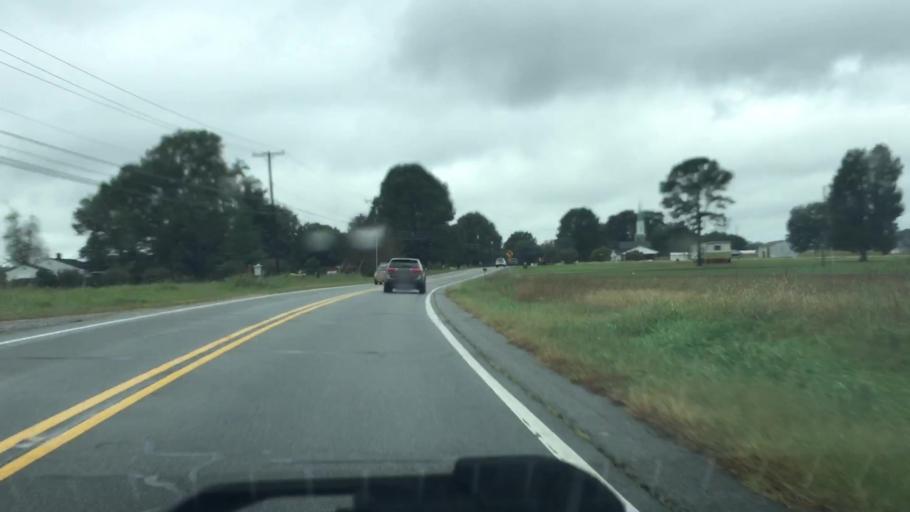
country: US
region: North Carolina
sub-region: Rowan County
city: China Grove
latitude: 35.6525
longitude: -80.5774
